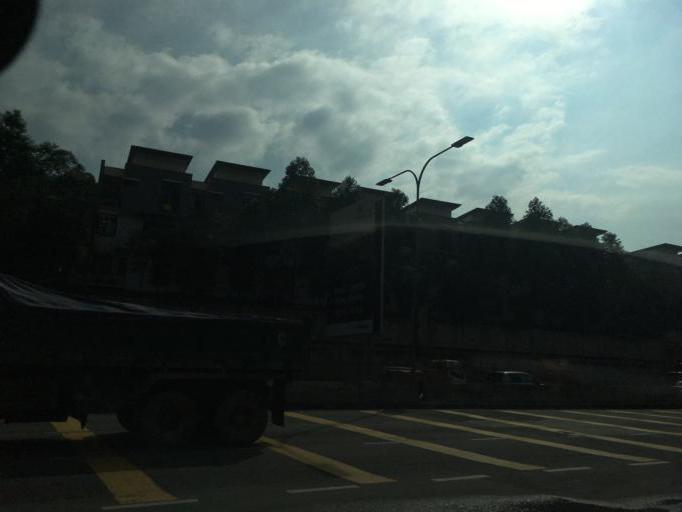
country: MY
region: Kuala Lumpur
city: Kuala Lumpur
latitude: 3.2228
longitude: 101.7315
